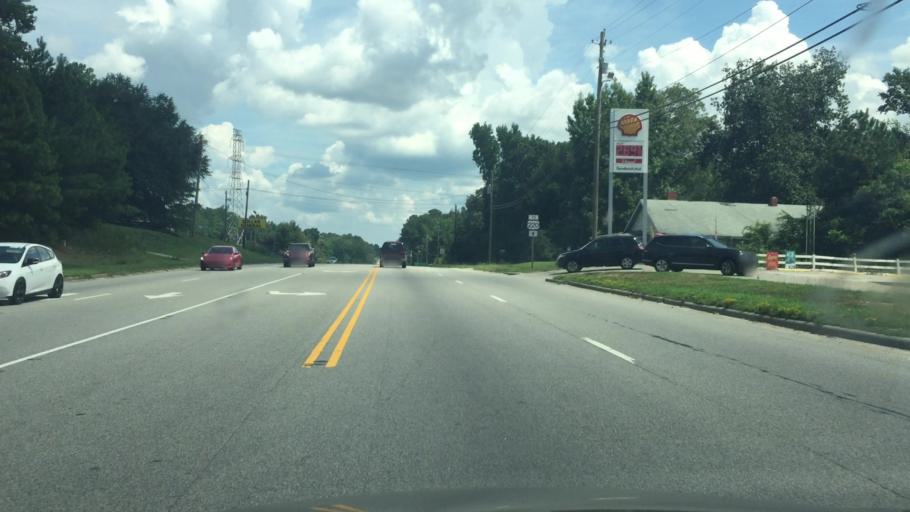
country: US
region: North Carolina
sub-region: Richmond County
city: East Rockingham
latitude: 34.9181
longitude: -79.7848
